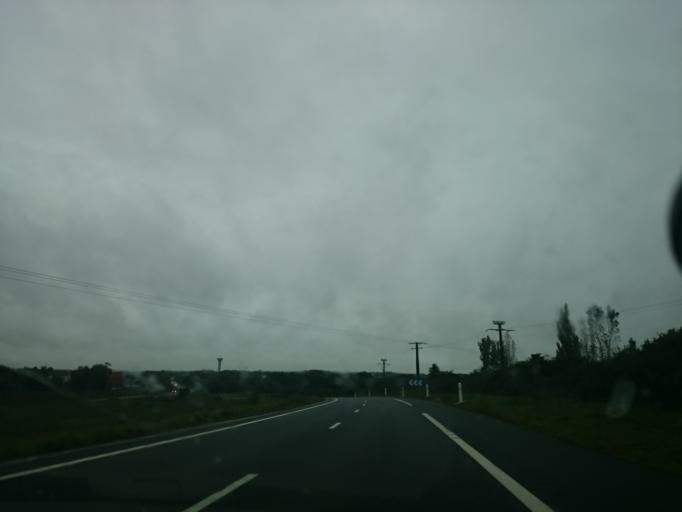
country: FR
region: Brittany
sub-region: Departement du Morbihan
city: Muzillac
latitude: 47.5687
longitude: -2.5163
